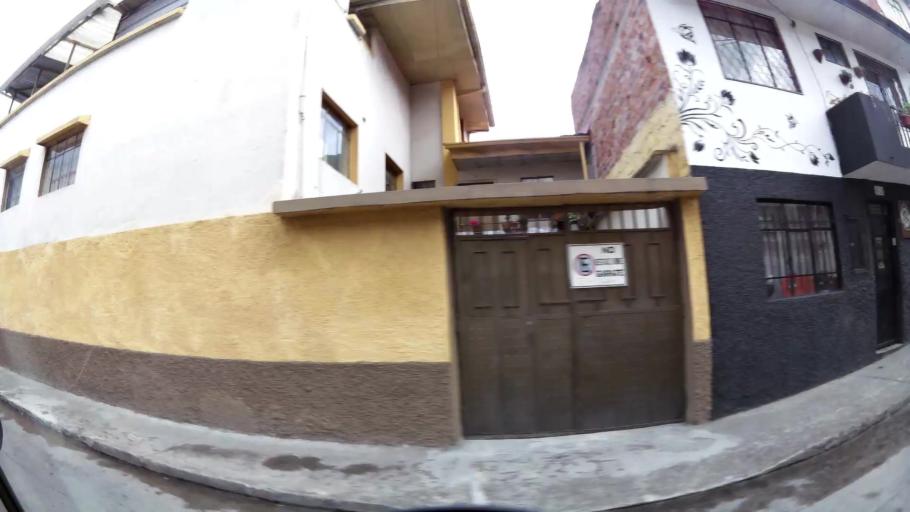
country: EC
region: Azuay
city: Cuenca
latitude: -2.8904
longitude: -79.0100
